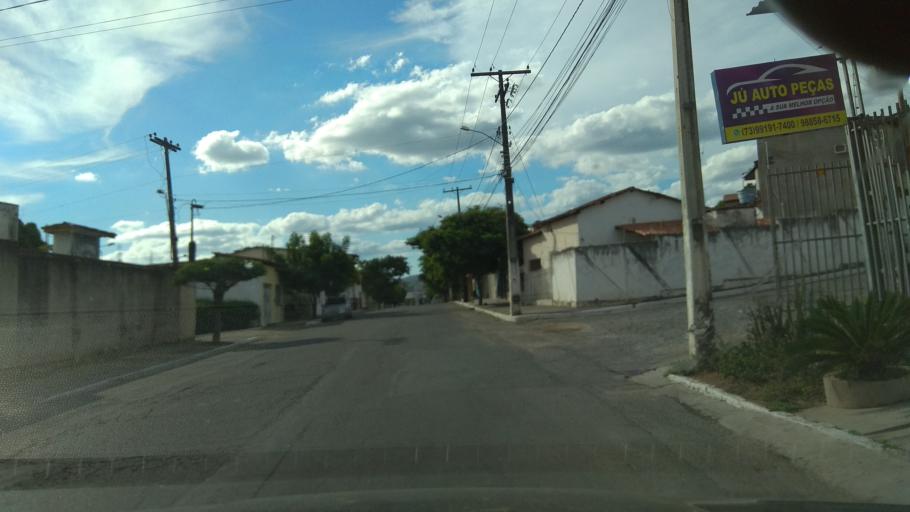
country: BR
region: Bahia
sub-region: Jequie
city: Jequie
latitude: -13.8709
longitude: -40.0758
